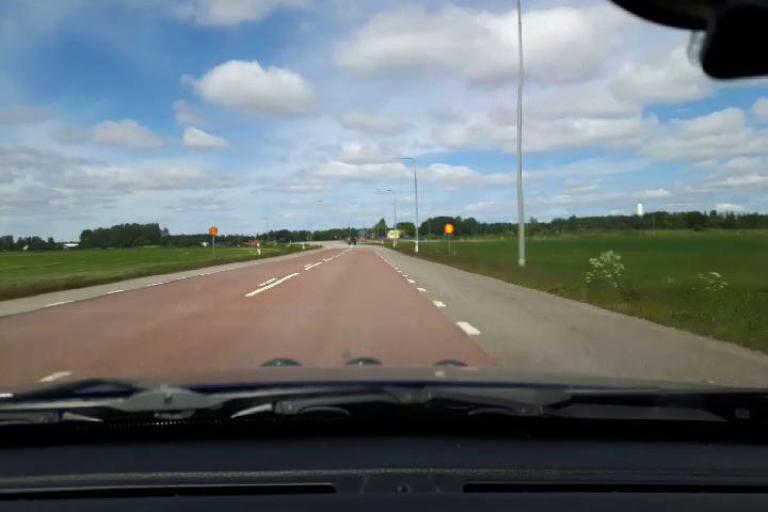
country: SE
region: Uppsala
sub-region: Osthammars Kommun
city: Bjorklinge
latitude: 60.0169
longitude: 17.5570
